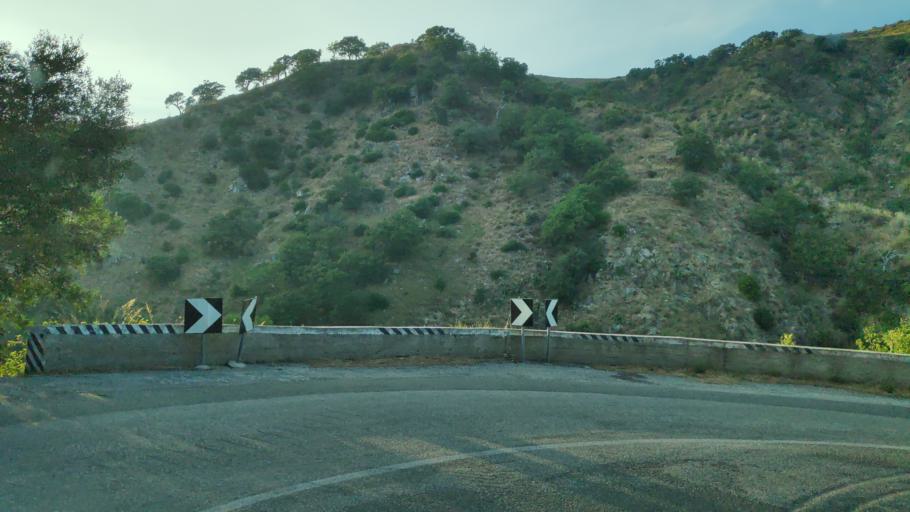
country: IT
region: Calabria
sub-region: Provincia di Catanzaro
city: Satriano
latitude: 38.6725
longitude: 16.4885
